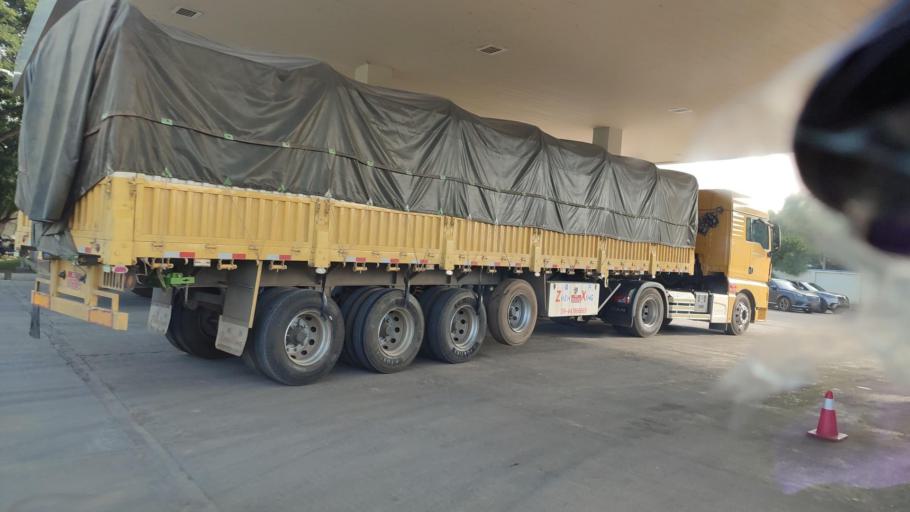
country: MM
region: Mandalay
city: Yamethin
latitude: 20.7534
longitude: 96.2587
